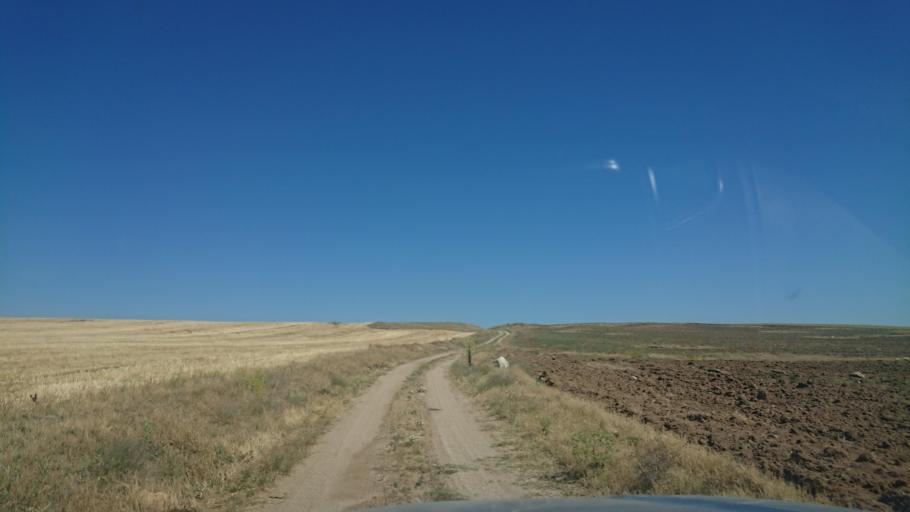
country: TR
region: Aksaray
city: Sariyahsi
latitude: 38.9286
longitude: 33.8496
